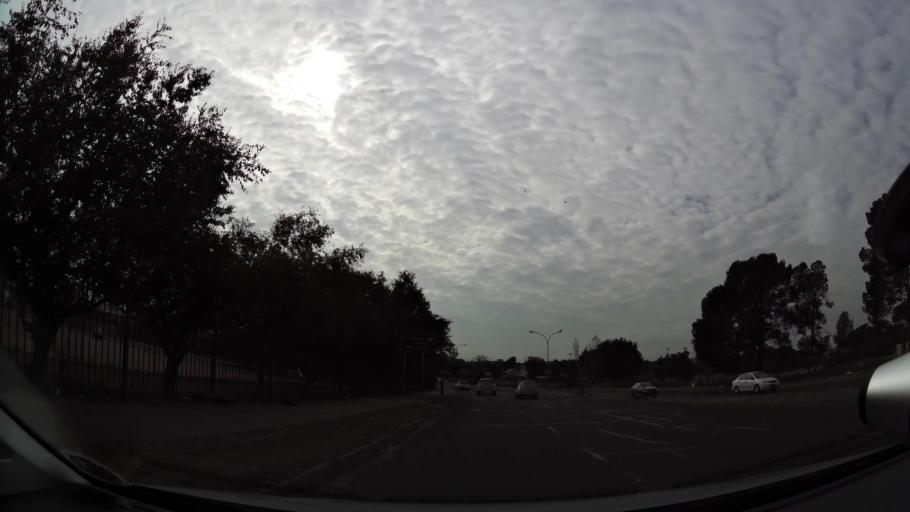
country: ZA
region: Orange Free State
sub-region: Mangaung Metropolitan Municipality
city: Bloemfontein
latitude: -29.1258
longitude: 26.2105
